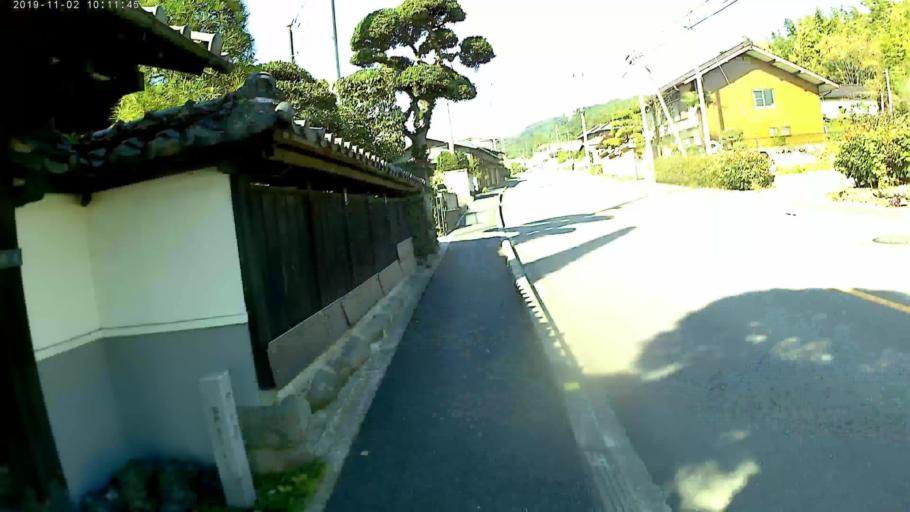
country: JP
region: Gunma
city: Annaka
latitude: 36.3171
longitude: 138.7909
